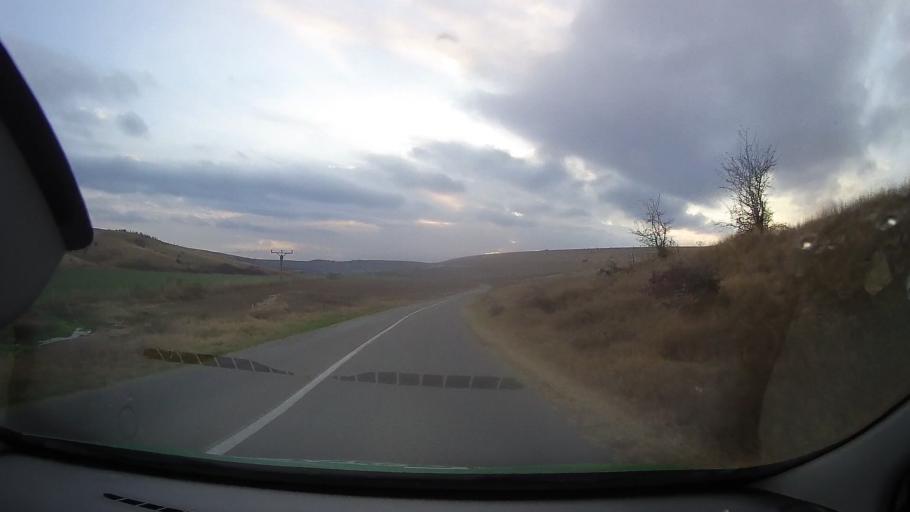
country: RO
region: Constanta
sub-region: Comuna Dobromir
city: Dobromir
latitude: 44.0315
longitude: 27.8005
